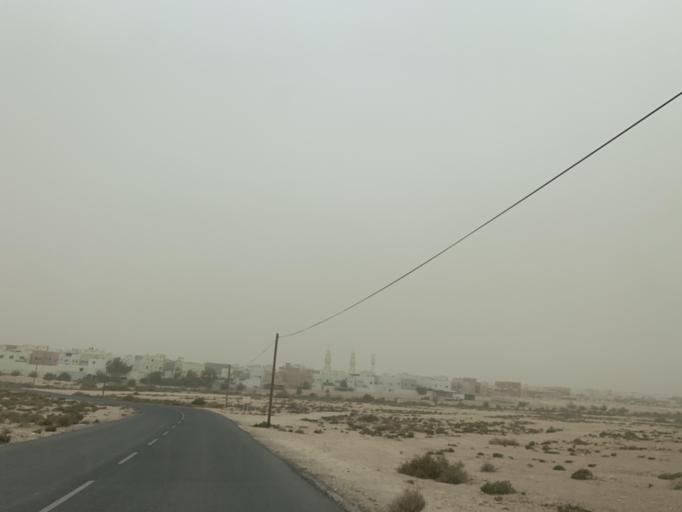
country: BH
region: Central Governorate
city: Madinat Hamad
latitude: 26.1281
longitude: 50.5169
